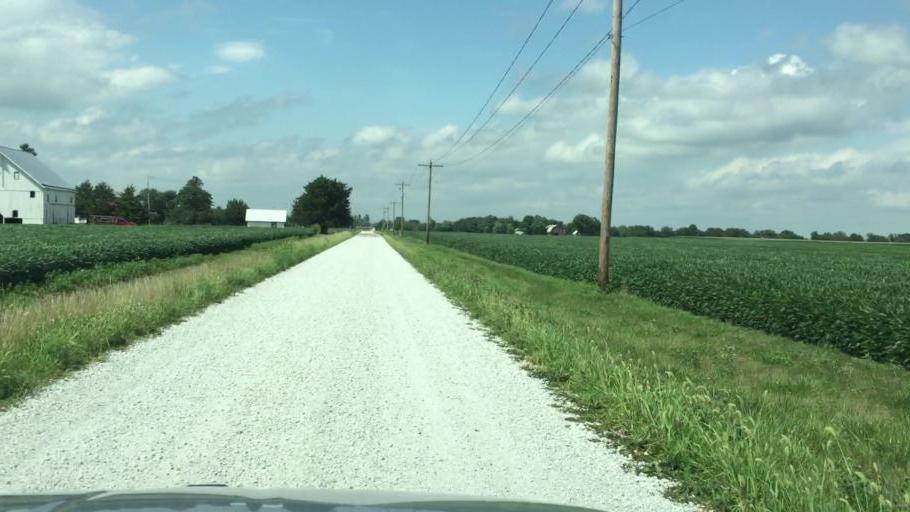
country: US
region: Illinois
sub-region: Hancock County
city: Carthage
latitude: 40.5320
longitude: -91.1575
